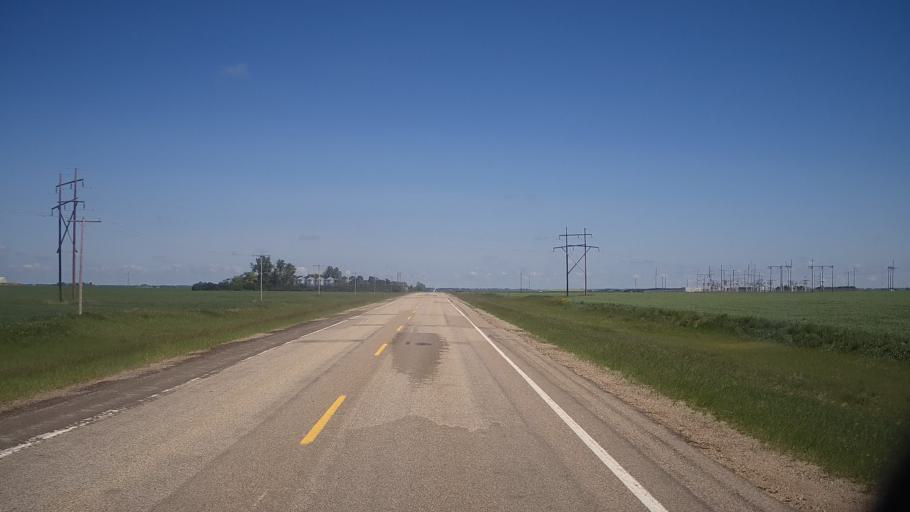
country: CA
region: Saskatchewan
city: Saskatoon
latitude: 51.9773
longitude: -106.0754
